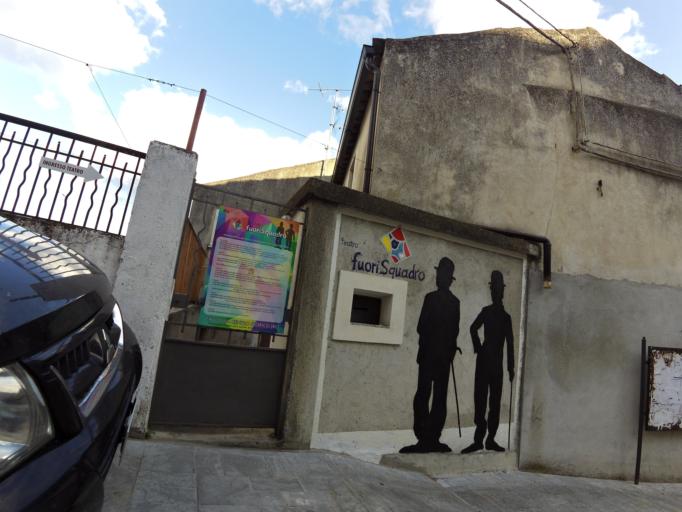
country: IT
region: Calabria
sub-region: Provincia di Reggio Calabria
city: Caulonia
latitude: 38.3811
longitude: 16.4075
